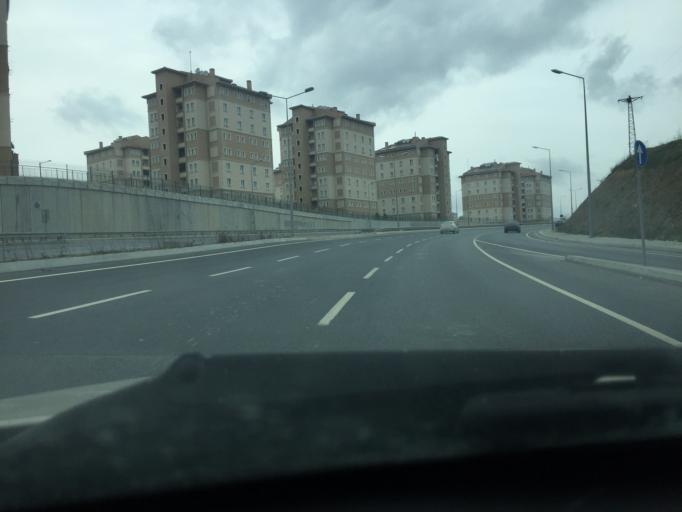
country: TR
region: Istanbul
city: Basaksehir
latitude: 41.1353
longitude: 28.7910
